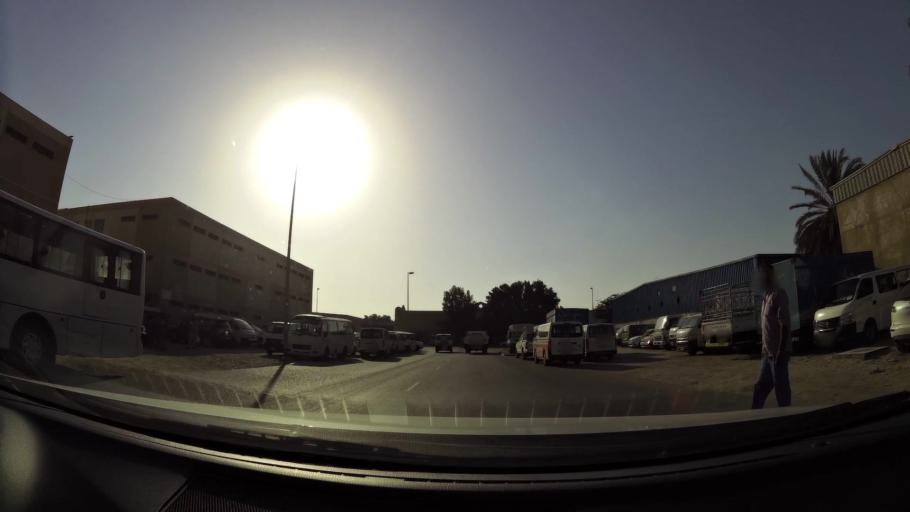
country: AE
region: Dubai
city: Dubai
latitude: 25.1334
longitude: 55.2490
